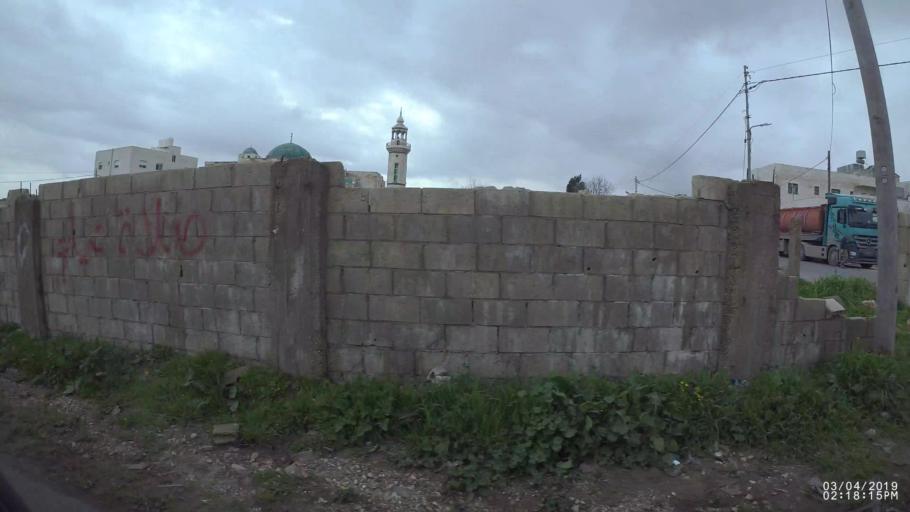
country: JO
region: Amman
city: Wadi as Sir
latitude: 31.9412
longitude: 35.8324
